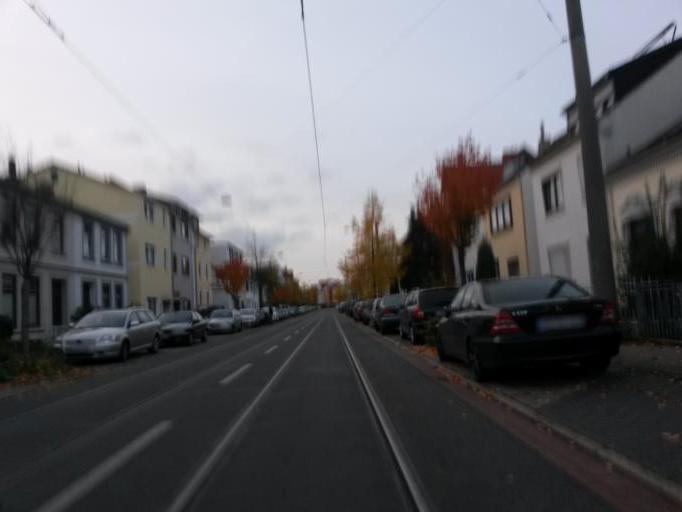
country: DE
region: Bremen
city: Bremen
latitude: 53.0649
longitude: 8.8639
